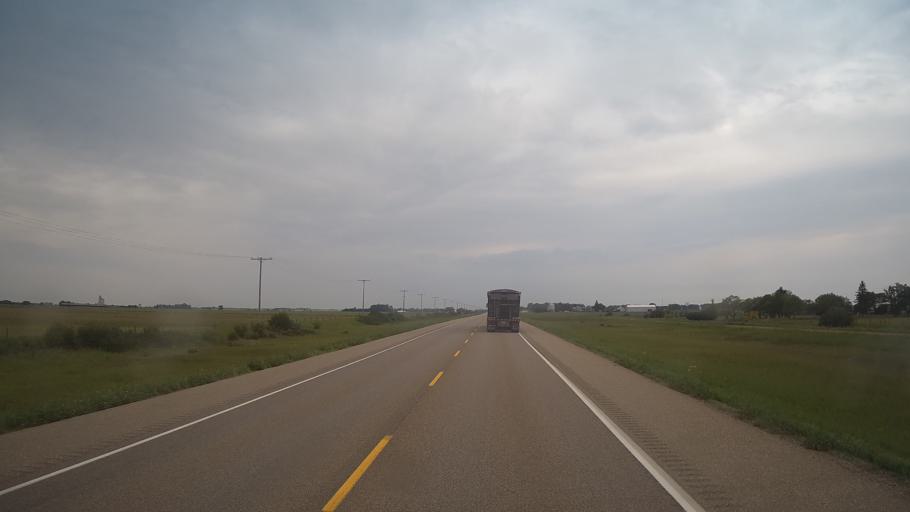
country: CA
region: Saskatchewan
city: Langham
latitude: 52.1289
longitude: -107.1891
